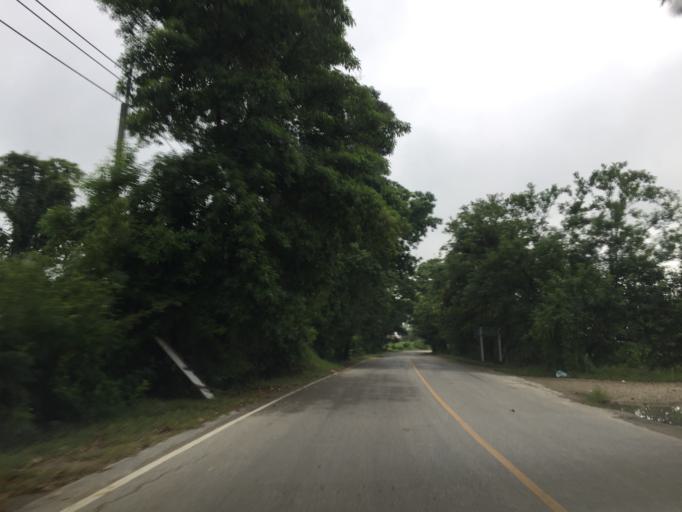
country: TH
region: Lamphun
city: Ban Thi
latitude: 18.6698
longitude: 99.0918
